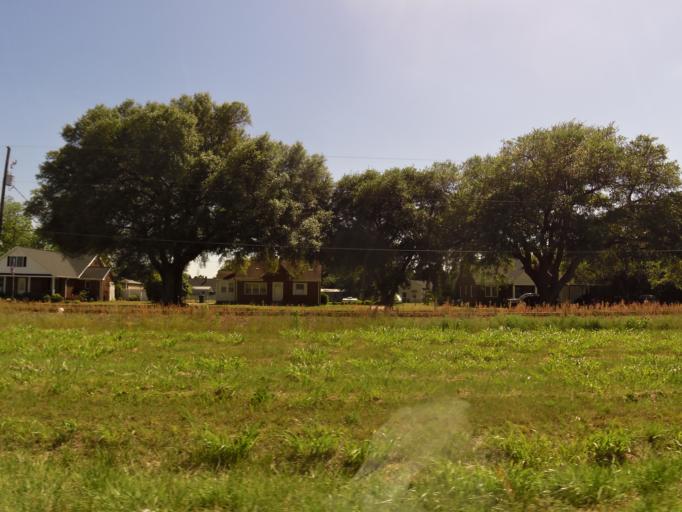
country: US
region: South Carolina
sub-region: Aiken County
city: Aiken
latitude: 33.5310
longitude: -81.6410
